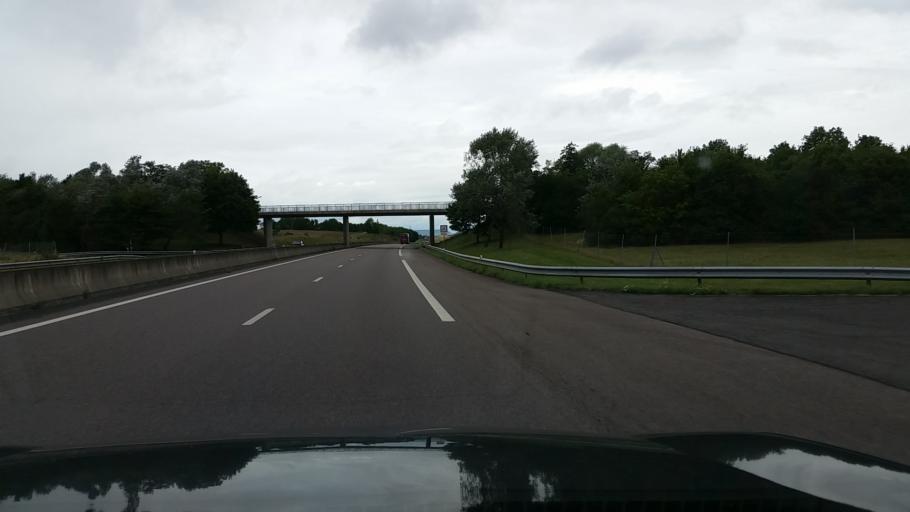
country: FR
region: Lorraine
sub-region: Departement de Meurthe-et-Moselle
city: Colombey-les-Belles
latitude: 48.5517
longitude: 5.8933
